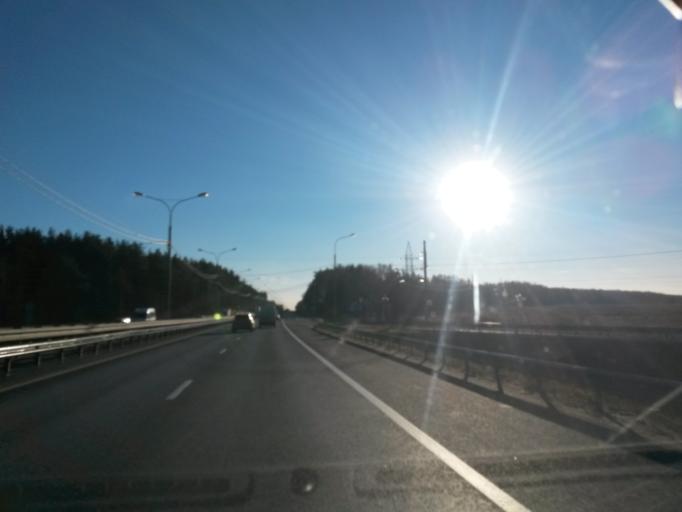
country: RU
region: Moskovskaya
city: Kostino
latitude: 56.0433
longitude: 37.8935
